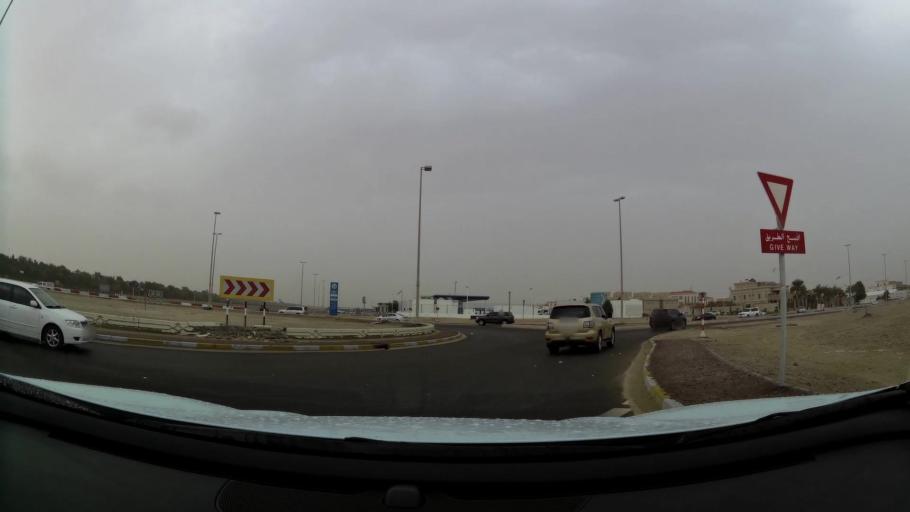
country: AE
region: Abu Dhabi
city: Abu Dhabi
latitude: 24.4061
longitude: 54.6057
